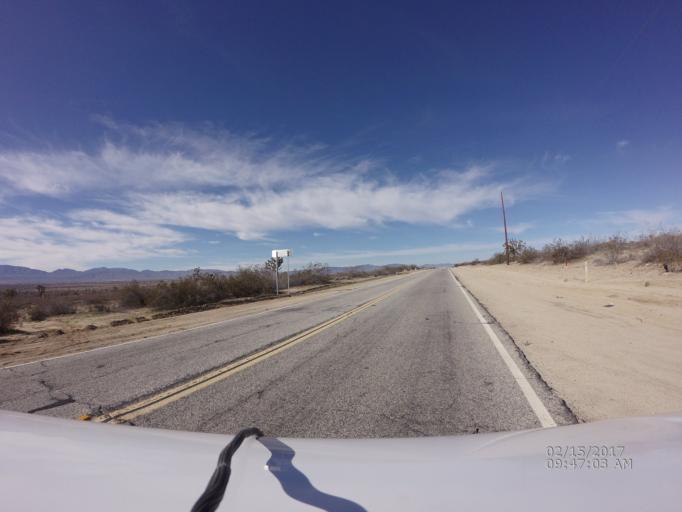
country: US
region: California
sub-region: Los Angeles County
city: Lake Los Angeles
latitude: 34.6166
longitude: -117.8991
